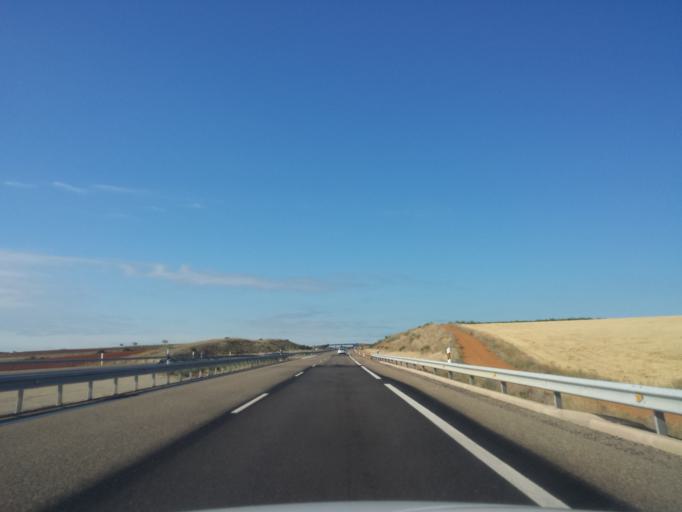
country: ES
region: Castille and Leon
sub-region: Provincia de Leon
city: Villamanan
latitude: 42.3512
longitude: -5.6010
